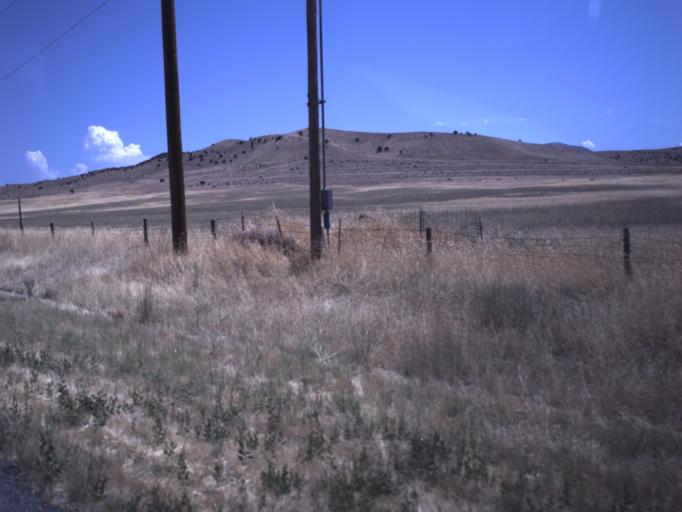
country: US
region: Utah
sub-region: Millard County
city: Delta
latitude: 39.4288
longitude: -112.3250
